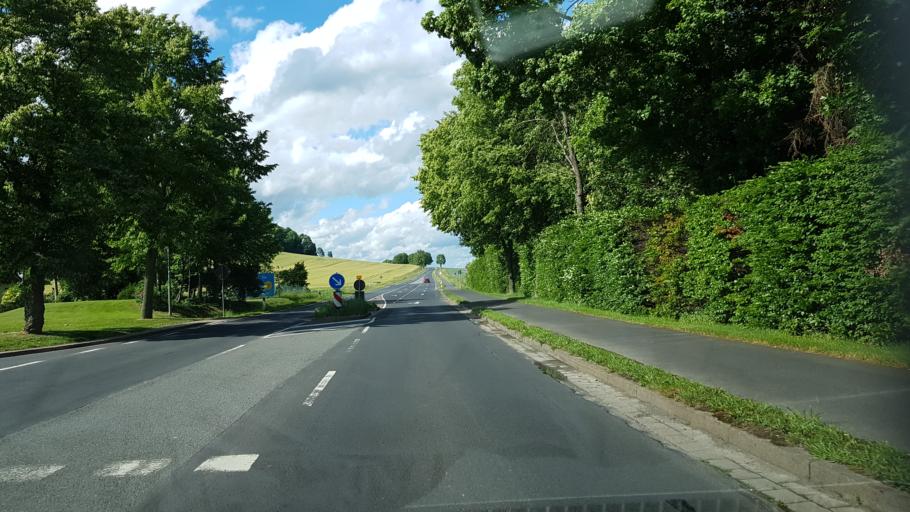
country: DE
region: Lower Saxony
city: Hardegsen
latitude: 51.6011
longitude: 9.8535
